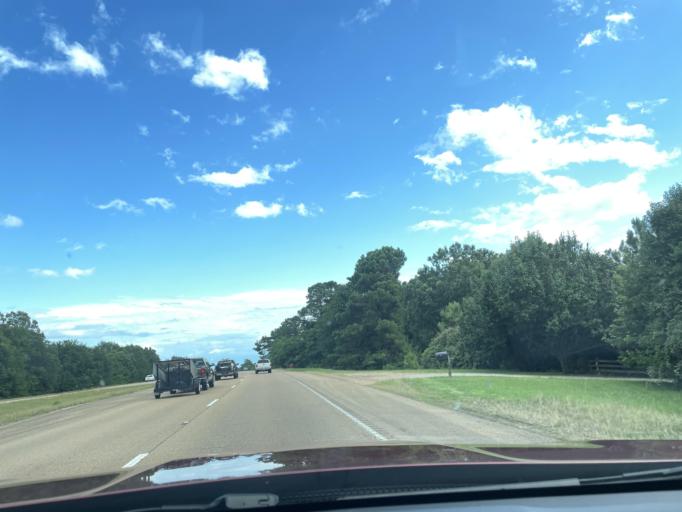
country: US
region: Mississippi
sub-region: Madison County
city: Flora
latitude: 32.5157
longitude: -90.3055
